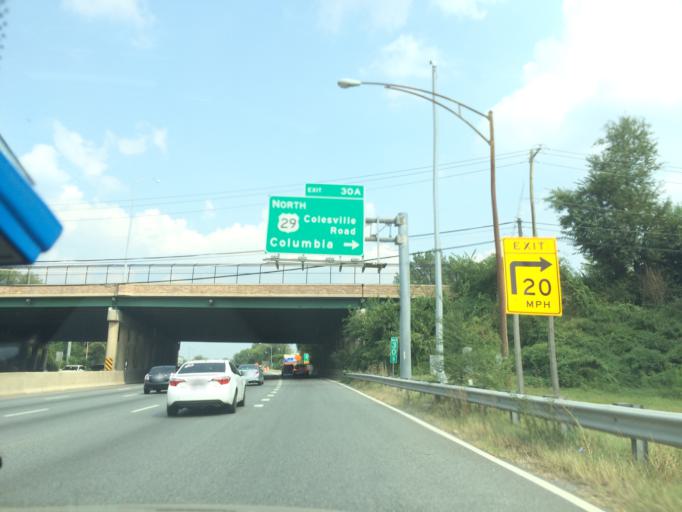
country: US
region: Maryland
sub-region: Montgomery County
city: Four Corners
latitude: 39.0158
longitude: -77.0176
